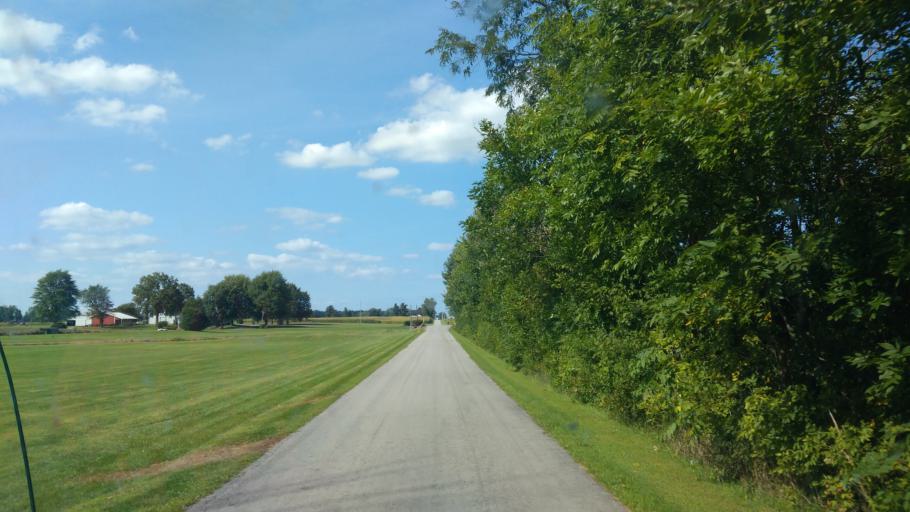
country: US
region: Ohio
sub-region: Hardin County
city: Forest
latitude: 40.7124
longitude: -83.4779
